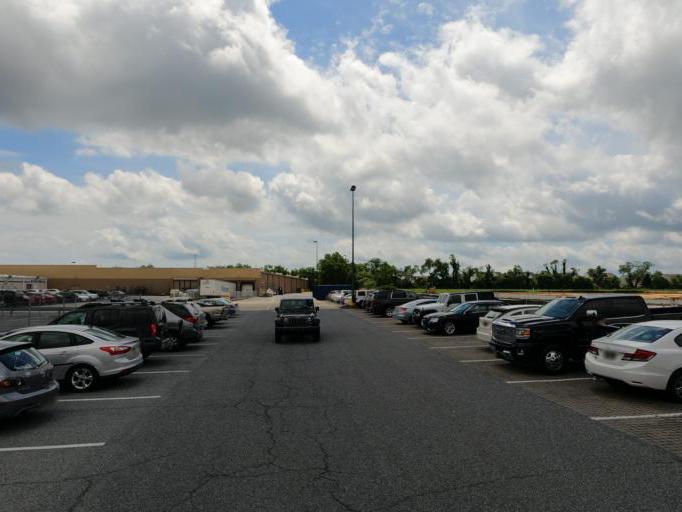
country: US
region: Delaware
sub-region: Sussex County
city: Lewes
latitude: 38.7280
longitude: -75.1341
